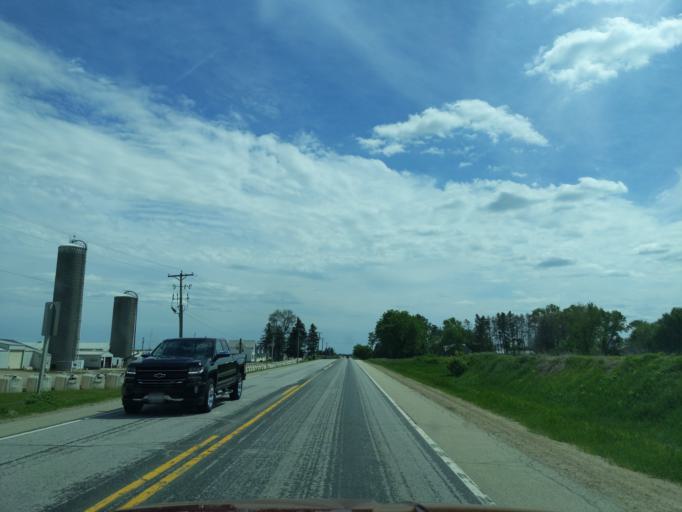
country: US
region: Wisconsin
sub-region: Dane County
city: De Forest
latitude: 43.2927
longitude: -89.3248
